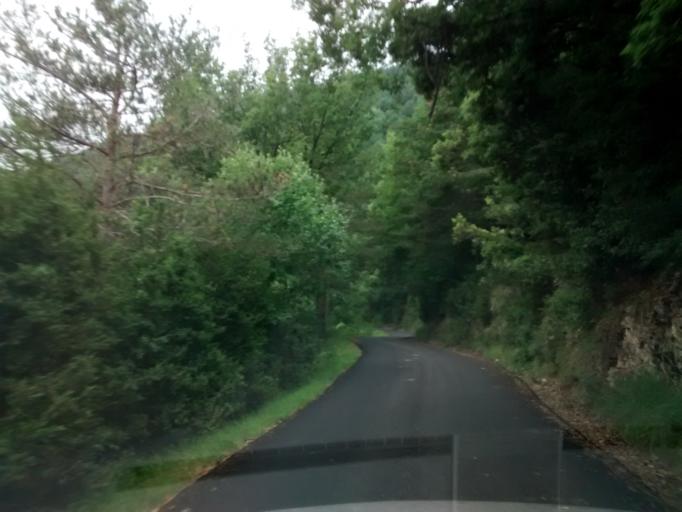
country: ES
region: Aragon
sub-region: Provincia de Huesca
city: Puertolas
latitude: 42.5683
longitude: 0.1401
